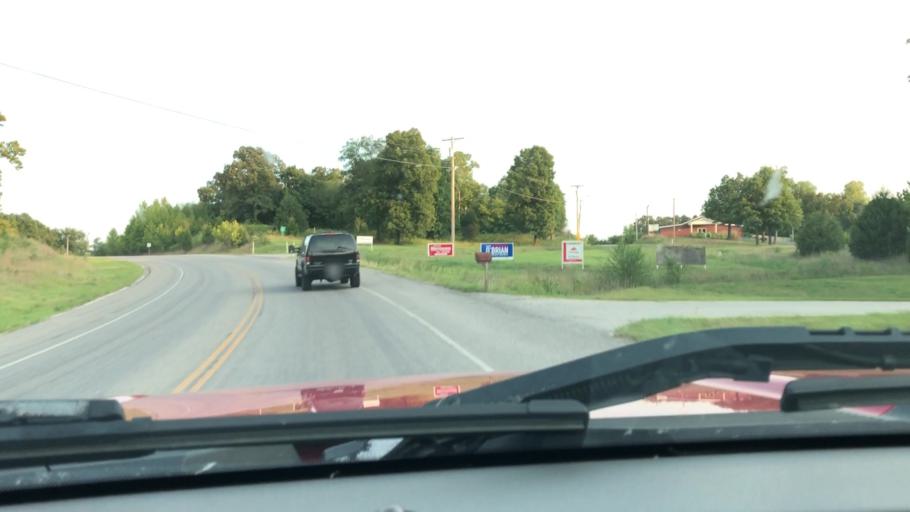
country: US
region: Missouri
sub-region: Jasper County
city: Joplin
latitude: 37.0260
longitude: -94.5153
